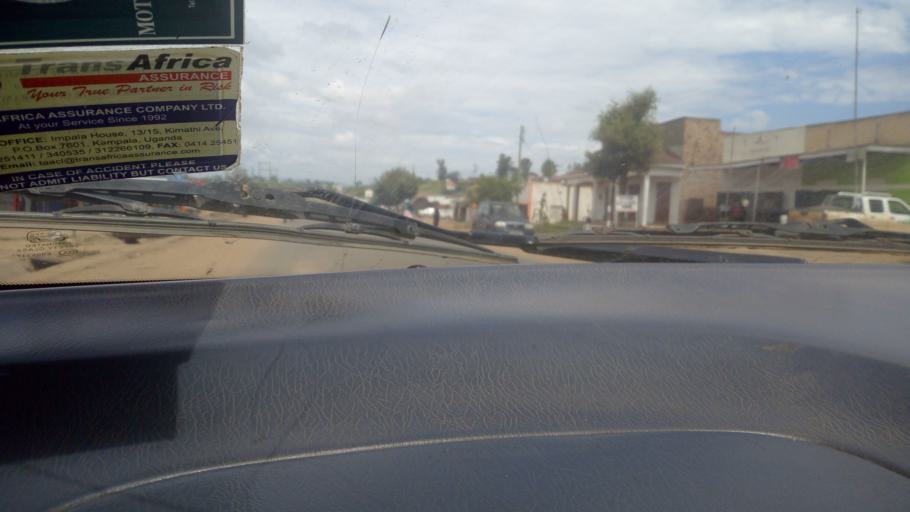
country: UG
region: Western Region
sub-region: Mbarara District
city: Bwizibwera
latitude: -0.4365
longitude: 30.5728
